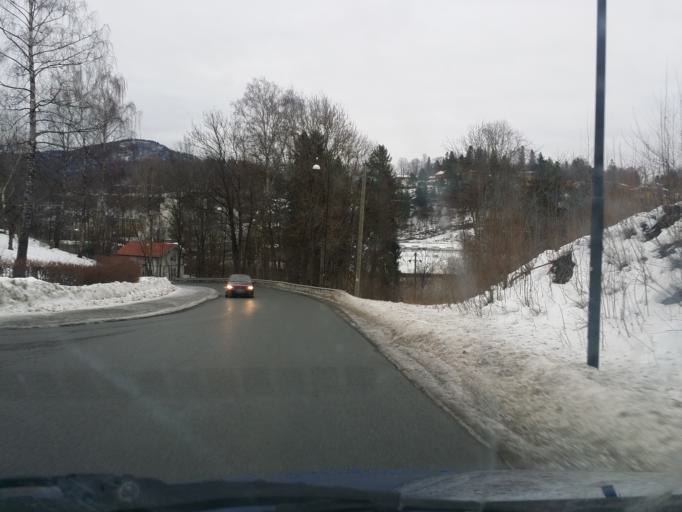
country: NO
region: Akershus
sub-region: Asker
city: Billingstad
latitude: 59.8971
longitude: 10.4949
